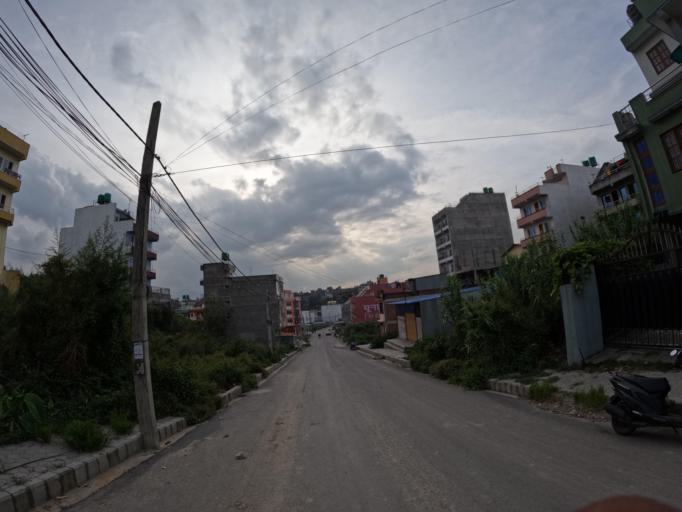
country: NP
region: Central Region
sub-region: Bagmati Zone
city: Bhaktapur
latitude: 27.6790
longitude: 85.3919
